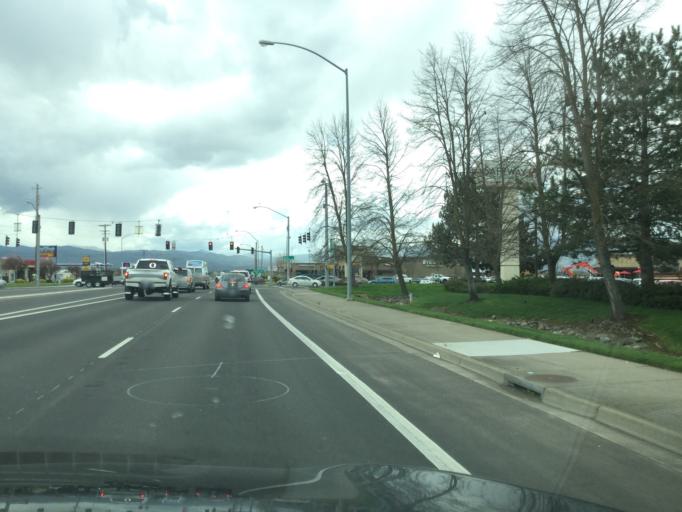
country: US
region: Oregon
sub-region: Jackson County
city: Medford
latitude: 42.3615
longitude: -122.8582
